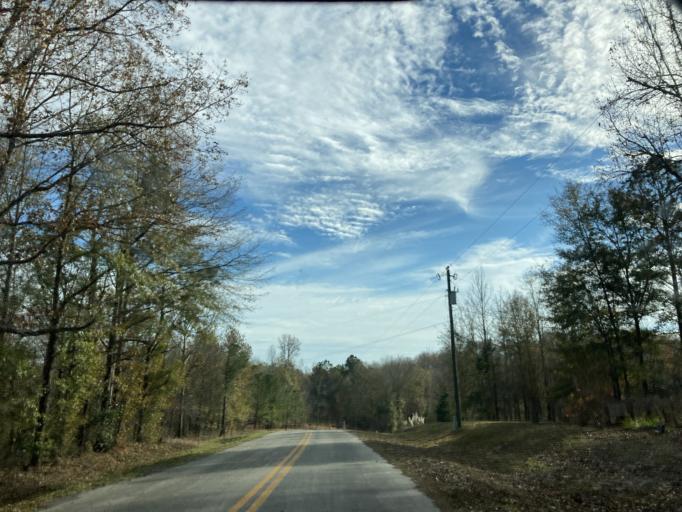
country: US
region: Georgia
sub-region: Jones County
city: Gray
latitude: 32.9122
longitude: -83.5082
